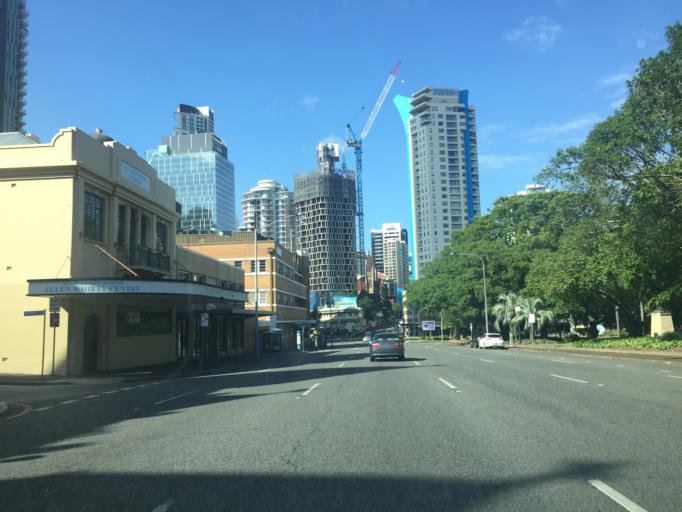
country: AU
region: Queensland
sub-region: Brisbane
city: Fortitude Valley
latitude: -27.4609
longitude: 153.0326
